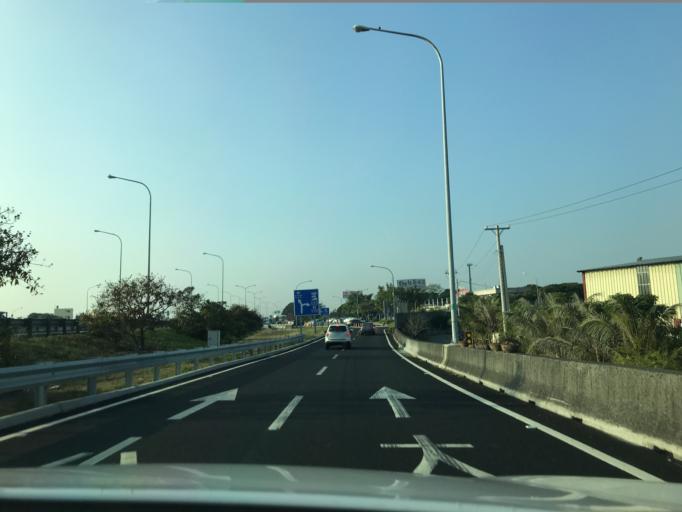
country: TW
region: Taiwan
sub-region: Yunlin
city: Douliu
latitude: 23.7902
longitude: 120.4788
